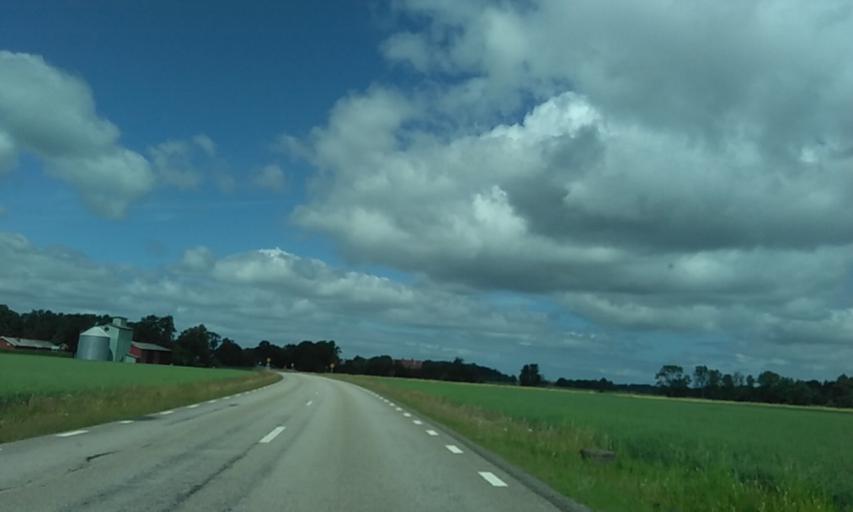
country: SE
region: Vaestra Goetaland
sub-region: Grastorps Kommun
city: Graestorp
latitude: 58.3031
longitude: 12.6715
